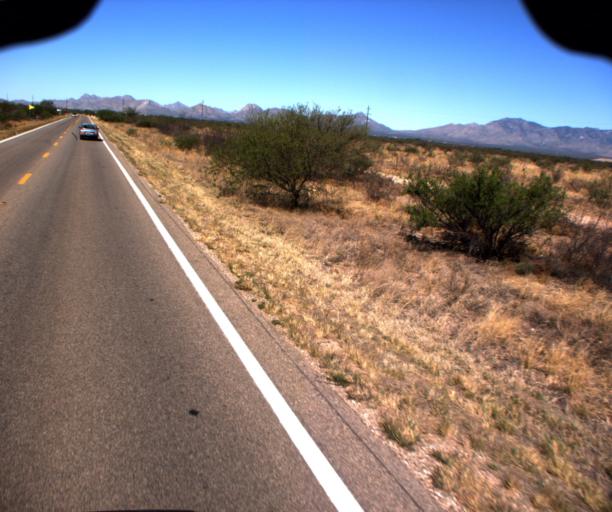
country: US
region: Arizona
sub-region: Cochise County
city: Huachuca City
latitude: 31.7092
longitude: -110.2769
